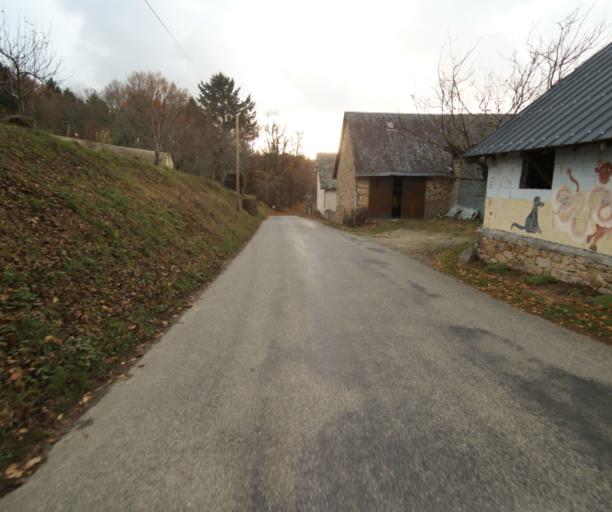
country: FR
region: Limousin
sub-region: Departement de la Correze
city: Sainte-Fortunade
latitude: 45.2099
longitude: 1.7766
